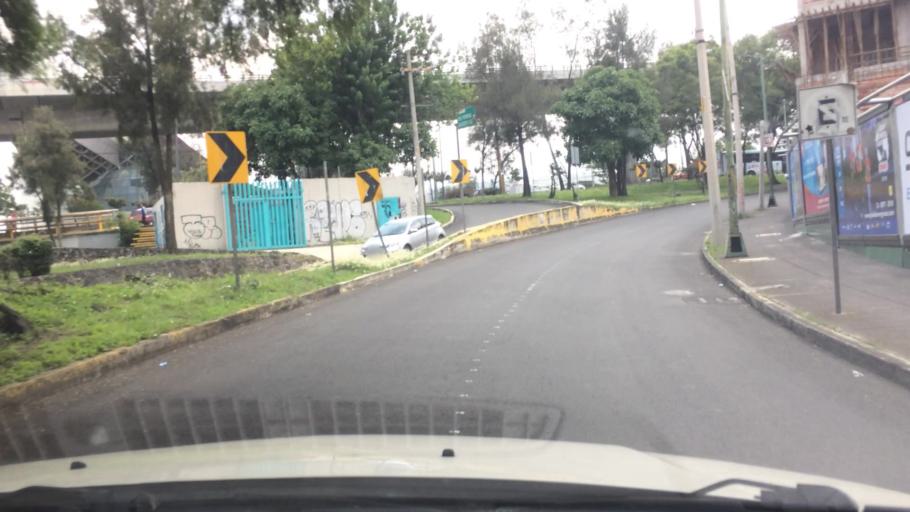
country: MX
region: Mexico City
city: Tlalpan
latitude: 19.3029
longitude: -99.1933
